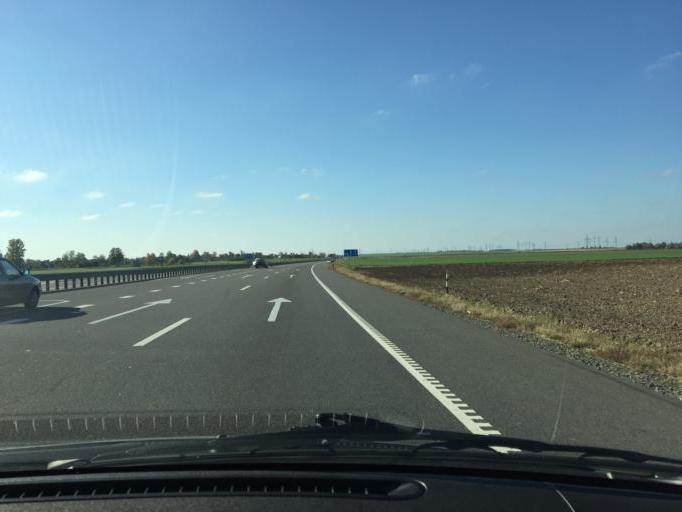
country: BY
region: Minsk
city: Slutsk
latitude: 53.0490
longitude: 27.5240
